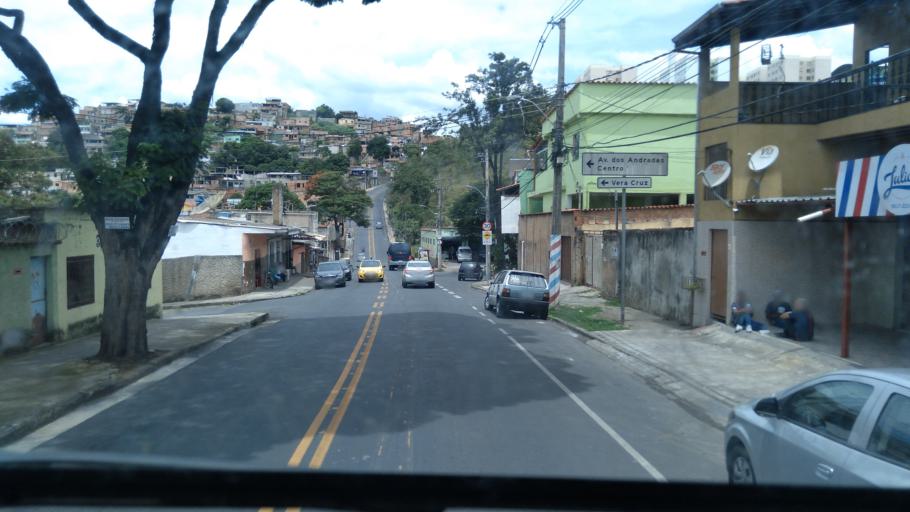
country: BR
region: Minas Gerais
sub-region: Belo Horizonte
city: Belo Horizonte
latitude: -19.9180
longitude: -43.8922
